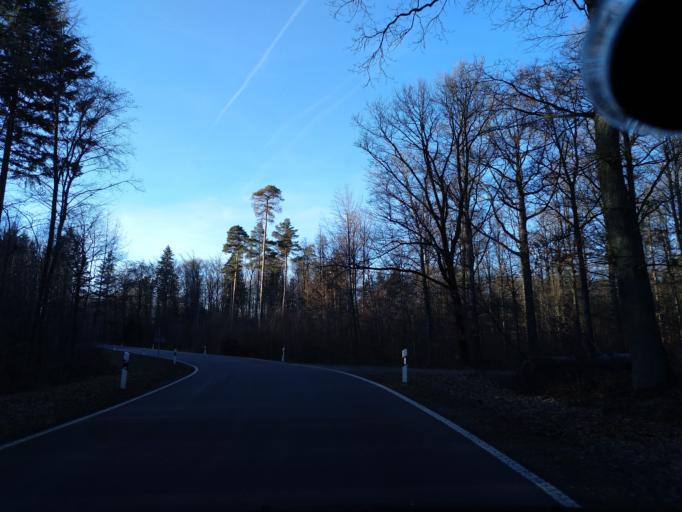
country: DE
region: Baden-Wuerttemberg
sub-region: Regierungsbezirk Stuttgart
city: Michelbach an der Bilz
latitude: 49.0804
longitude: 9.7966
